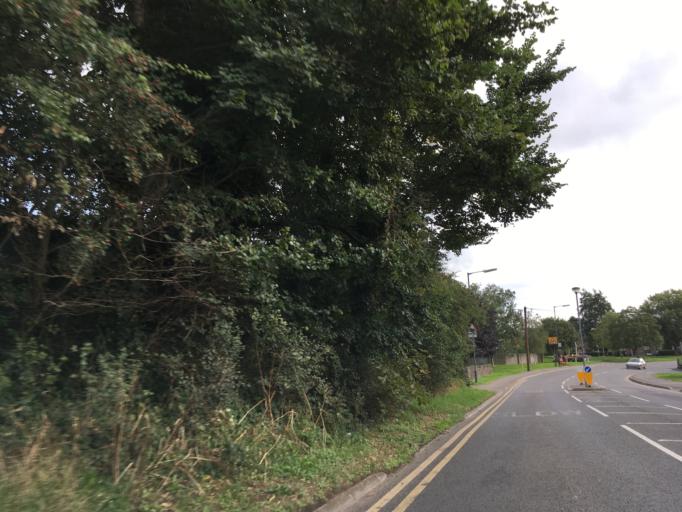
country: GB
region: England
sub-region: South Gloucestershire
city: Thornbury
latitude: 51.6177
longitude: -2.5149
